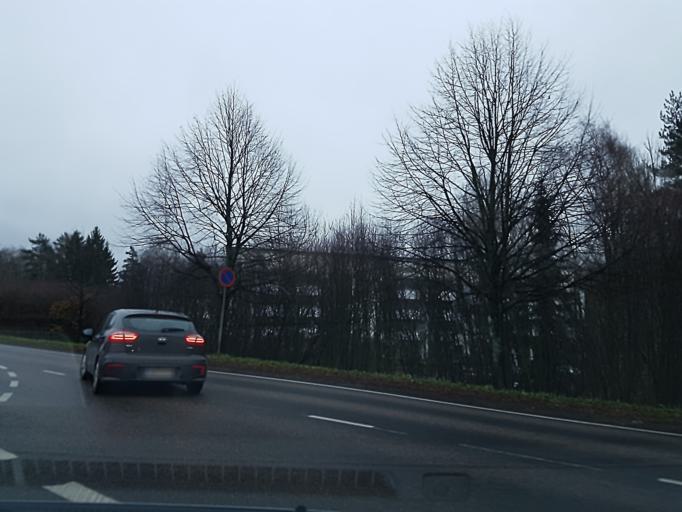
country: FI
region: Uusimaa
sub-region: Helsinki
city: Vantaa
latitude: 60.2354
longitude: 25.0831
